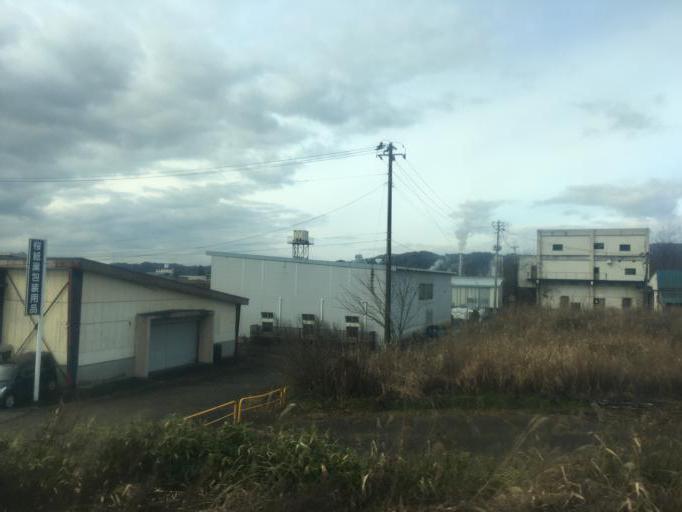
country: JP
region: Akita
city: Odate
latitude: 40.2951
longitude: 140.5662
